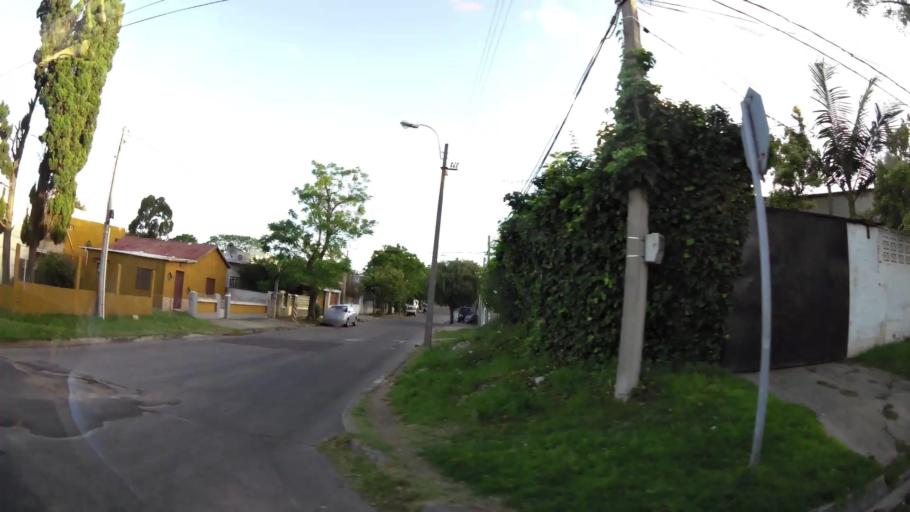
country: UY
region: Montevideo
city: Montevideo
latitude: -34.8837
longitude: -56.2539
